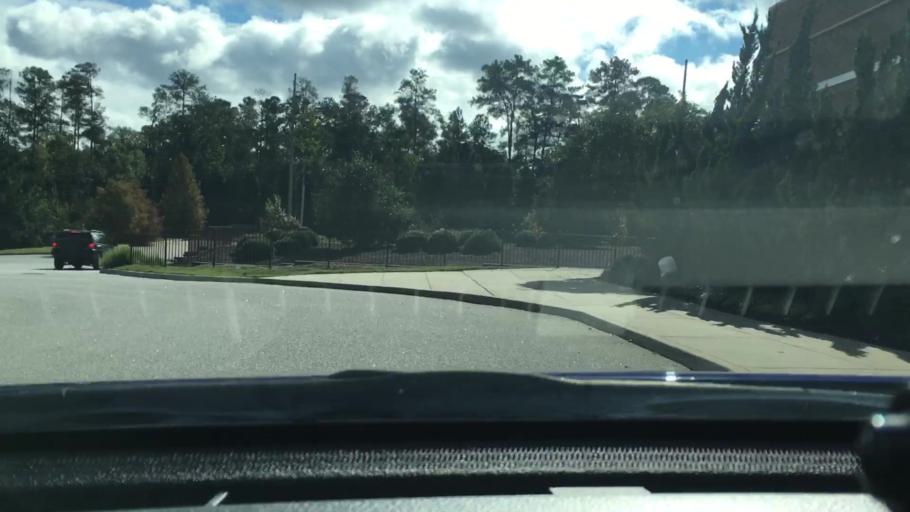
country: US
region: South Carolina
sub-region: Lexington County
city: Irmo
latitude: 34.0658
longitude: -81.1668
